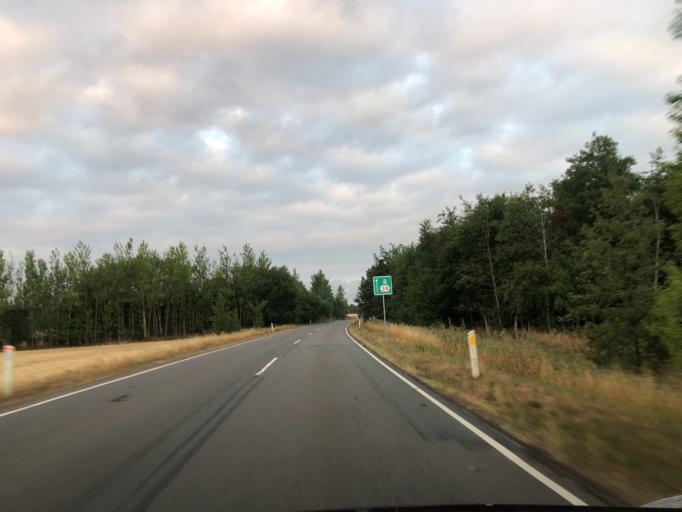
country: DK
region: Zealand
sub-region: Soro Kommune
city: Dianalund
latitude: 55.4560
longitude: 11.4450
